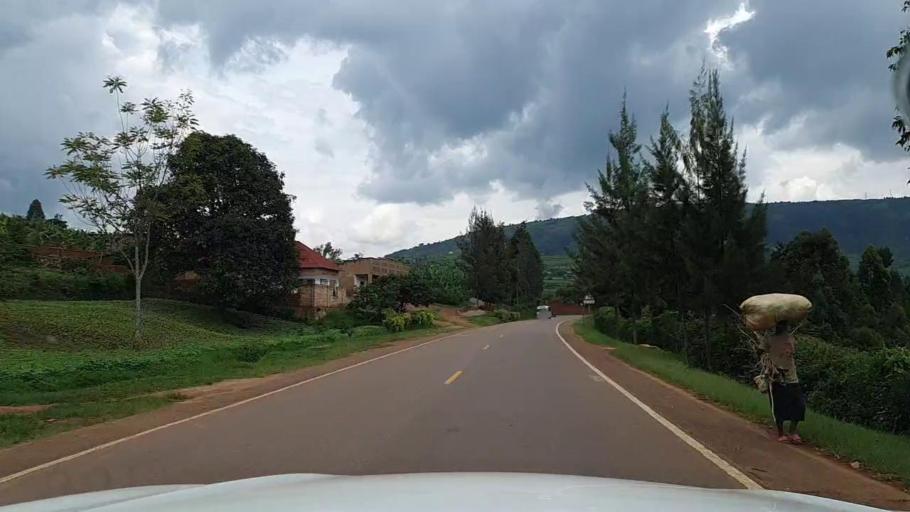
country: RW
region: Kigali
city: Kigali
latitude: -1.7837
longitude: 30.1299
